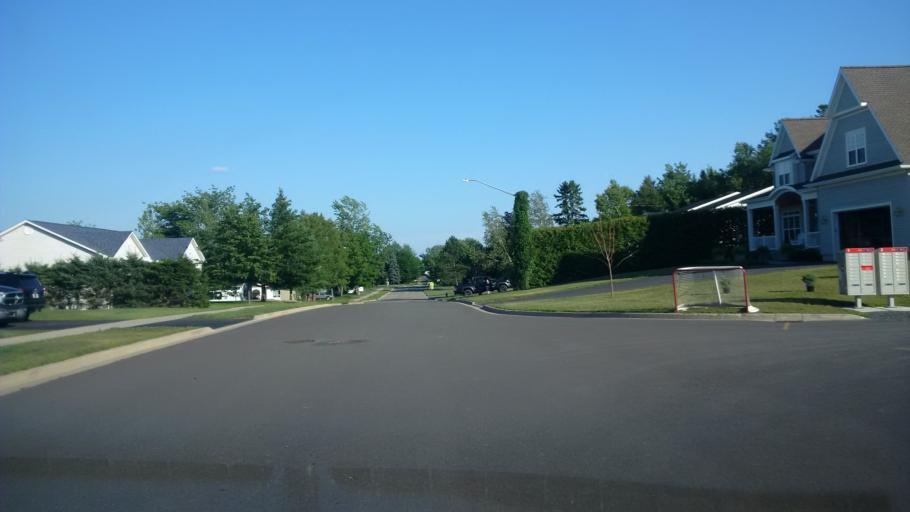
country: CA
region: New Brunswick
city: Fredericton
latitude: 45.8996
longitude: -66.6929
